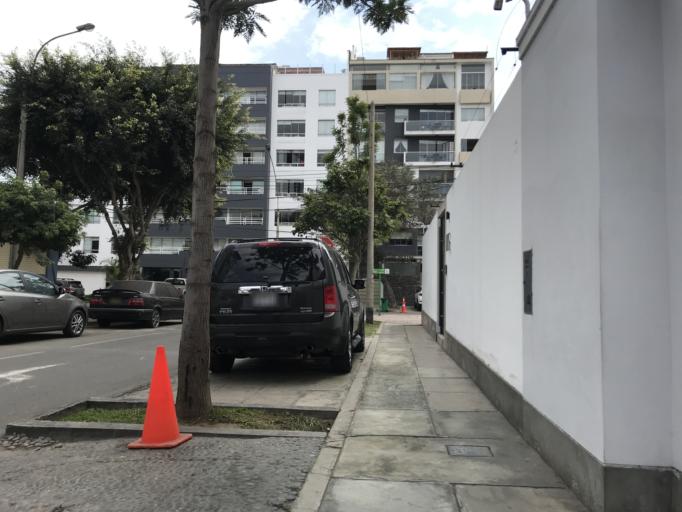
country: PE
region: Lima
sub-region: Lima
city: San Isidro
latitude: -12.1134
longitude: -77.0438
